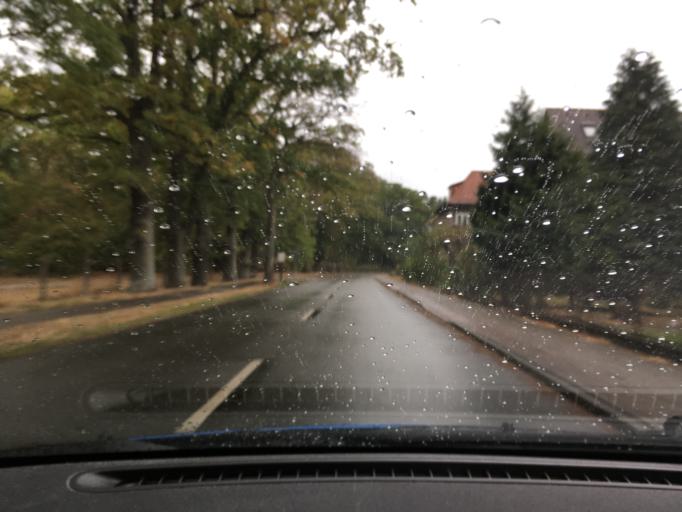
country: DE
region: Mecklenburg-Vorpommern
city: Domitz
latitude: 53.1477
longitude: 11.2416
